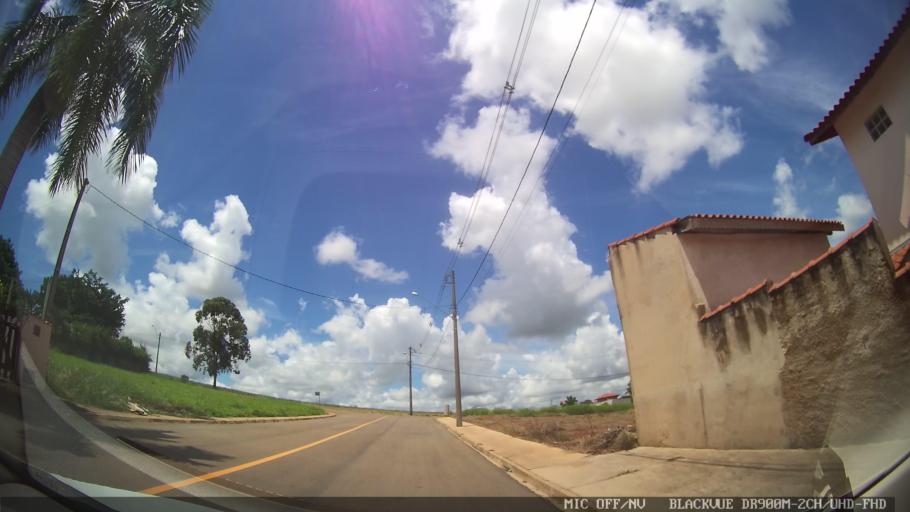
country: BR
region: Sao Paulo
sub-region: Amparo
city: Amparo
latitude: -22.8191
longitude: -46.6935
